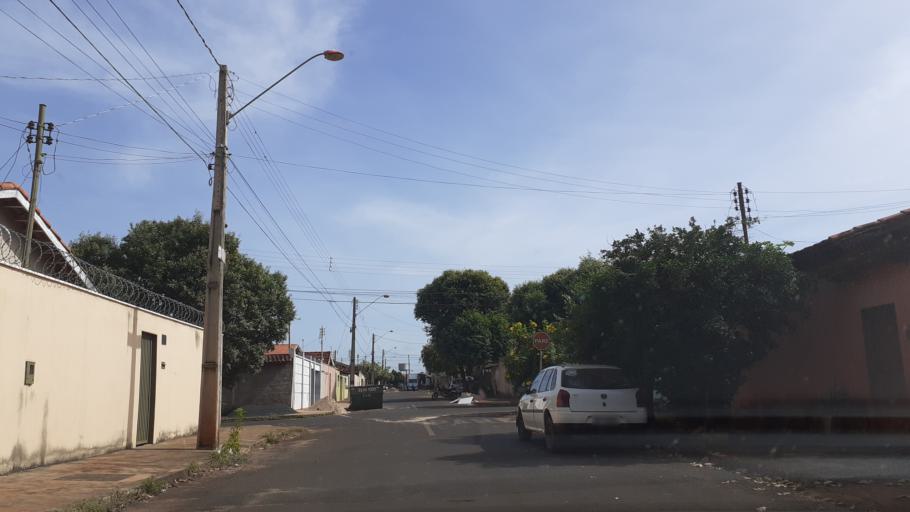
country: BR
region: Goias
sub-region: Itumbiara
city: Itumbiara
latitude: -18.4166
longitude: -49.2347
